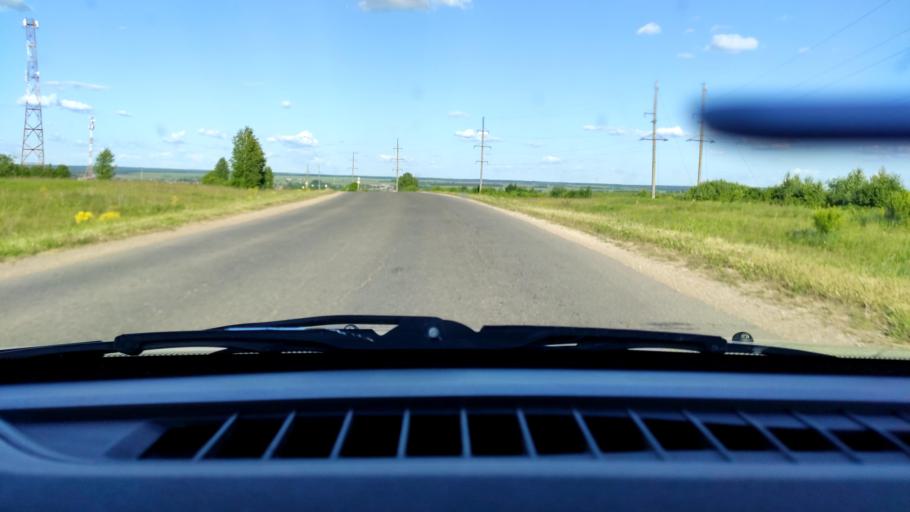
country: RU
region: Perm
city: Orda
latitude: 57.1885
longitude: 56.8754
